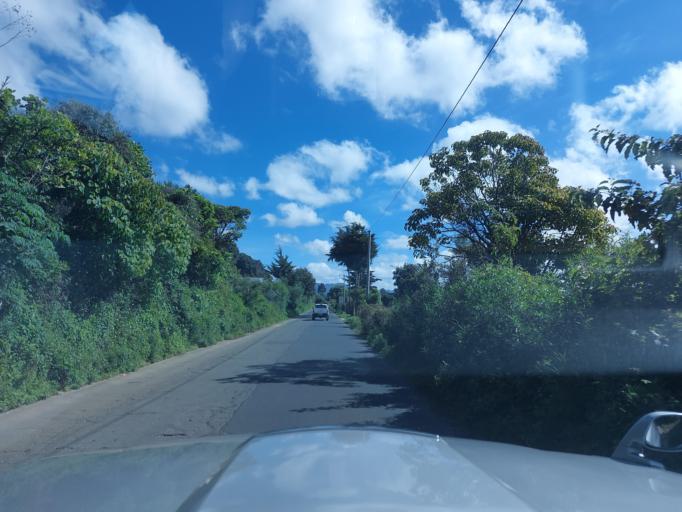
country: GT
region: Chimaltenango
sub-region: Municipio de Zaragoza
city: Zaragoza
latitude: 14.6547
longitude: -90.8970
